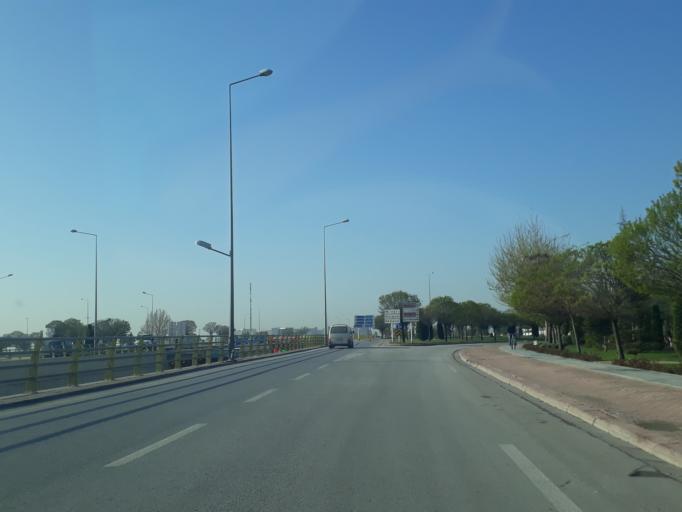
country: TR
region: Konya
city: Selcuklu
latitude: 37.8709
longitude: 32.5480
